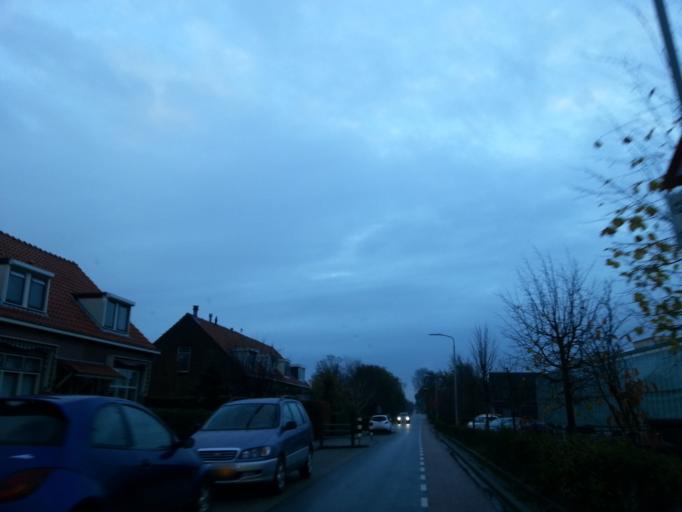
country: NL
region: South Holland
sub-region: Gemeente Pijnacker-Nootdorp
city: Pijnacker
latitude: 52.0163
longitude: 4.4219
